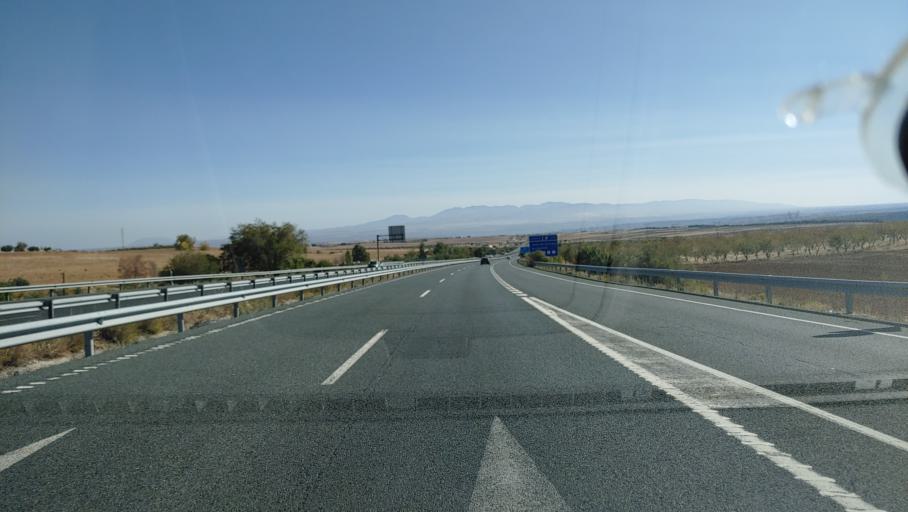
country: ES
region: Andalusia
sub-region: Provincia de Granada
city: Diezma
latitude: 37.3201
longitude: -3.3185
